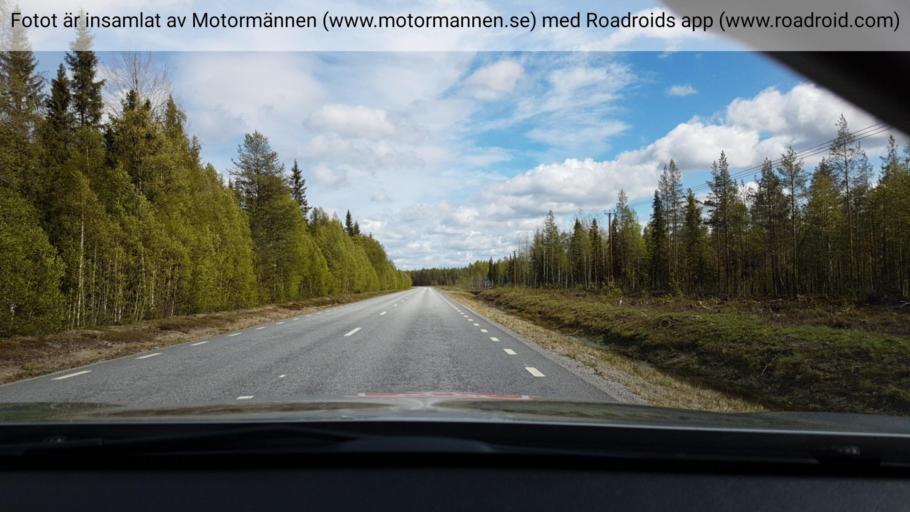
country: SE
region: Vaesterbotten
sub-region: Asele Kommun
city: Insjon
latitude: 64.1605
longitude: 17.8317
